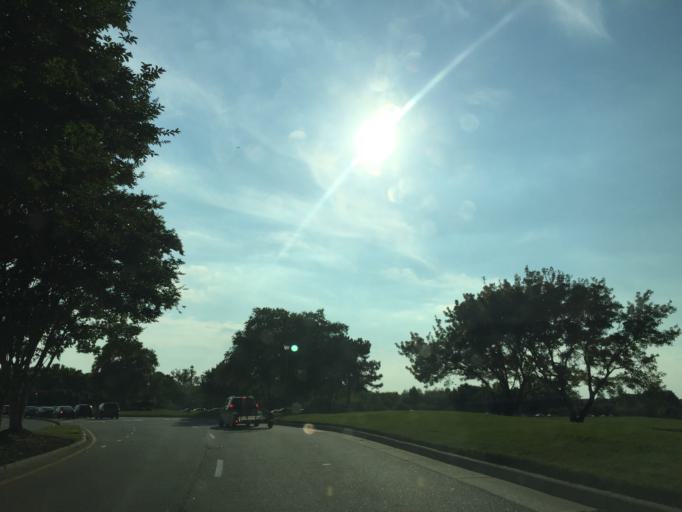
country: US
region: Virginia
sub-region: York County
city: Yorktown
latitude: 37.1217
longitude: -76.5049
